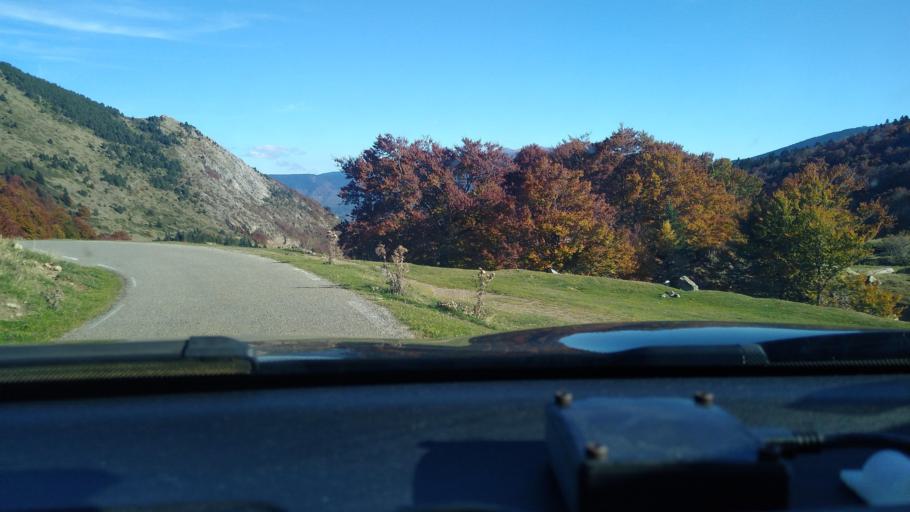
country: FR
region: Midi-Pyrenees
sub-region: Departement de l'Ariege
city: Ax-les-Thermes
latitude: 42.7289
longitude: 2.0123
